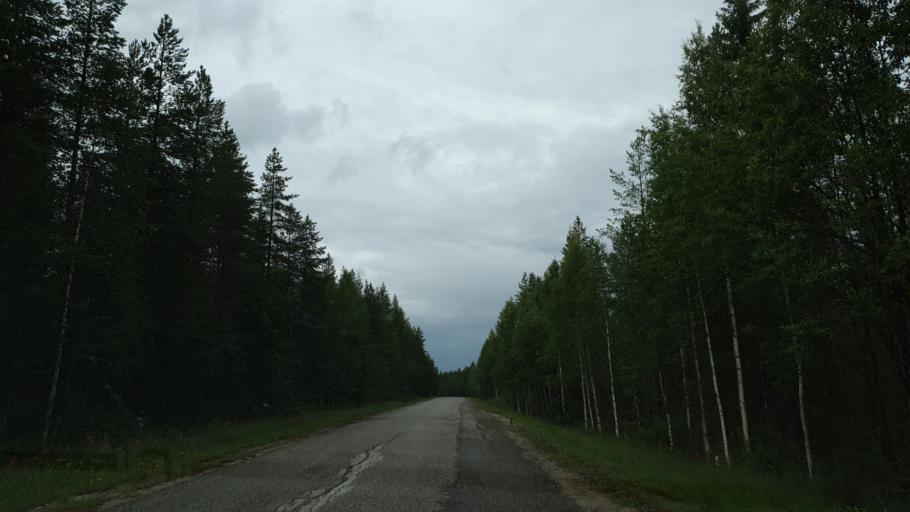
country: FI
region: Kainuu
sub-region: Kehys-Kainuu
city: Kuhmo
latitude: 64.4427
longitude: 29.7020
